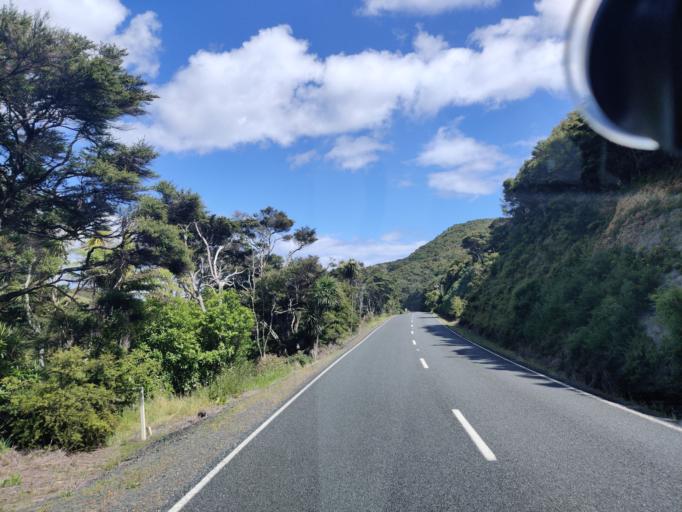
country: NZ
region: Northland
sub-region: Far North District
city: Paihia
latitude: -35.2653
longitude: 174.2697
